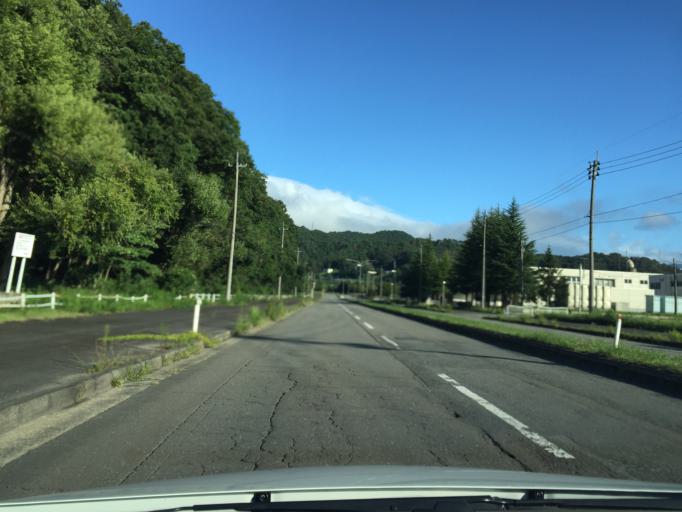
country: JP
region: Yamagata
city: Yonezawa
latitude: 37.9115
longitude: 140.1702
